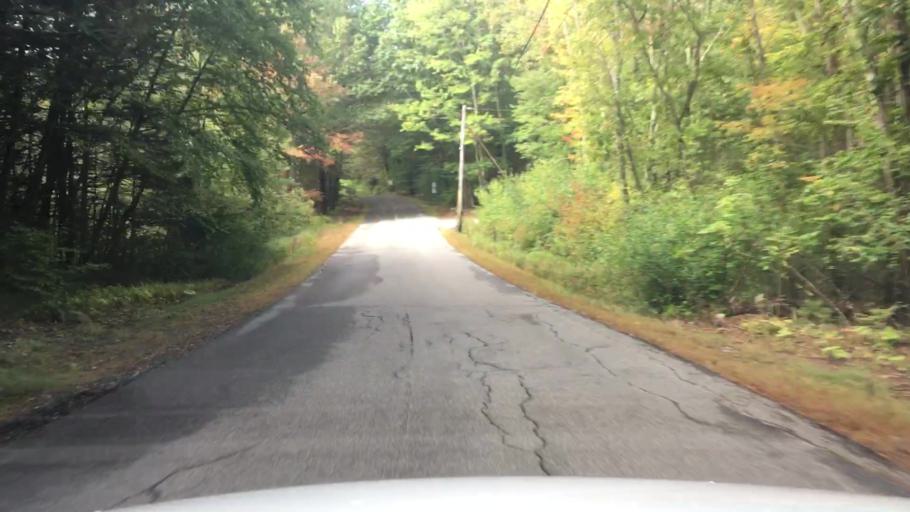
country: US
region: Maine
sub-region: York County
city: York Harbor
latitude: 43.1193
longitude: -70.6795
